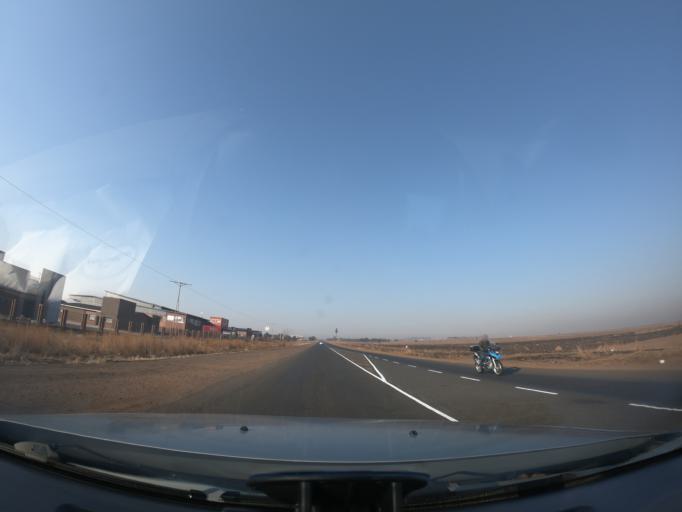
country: ZA
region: Mpumalanga
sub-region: Nkangala District Municipality
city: Middelburg
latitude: -25.8097
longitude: 29.4619
